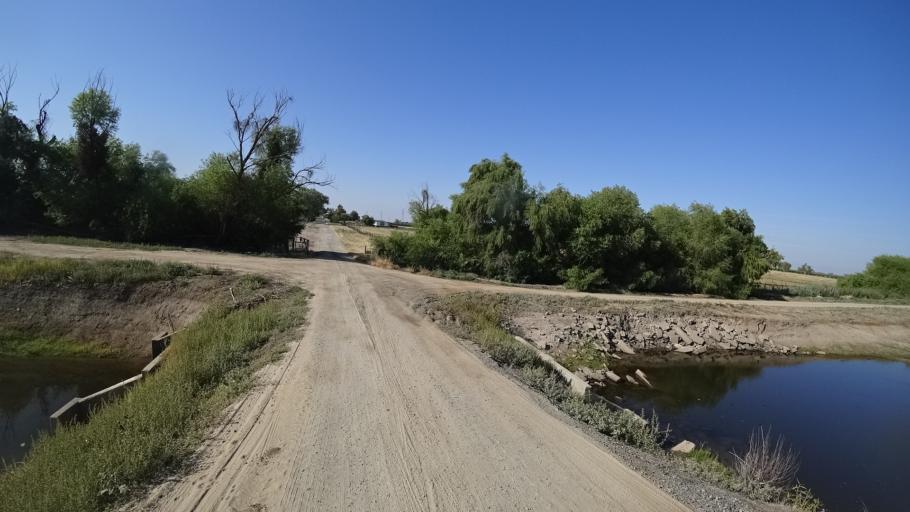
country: US
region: California
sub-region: Fresno County
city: Riverdale
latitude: 36.3819
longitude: -119.8872
